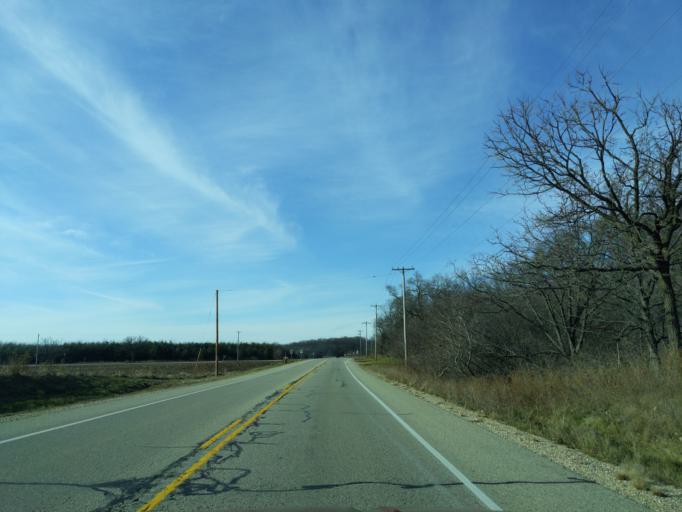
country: US
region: Wisconsin
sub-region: Jefferson County
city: Palmyra
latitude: 42.7976
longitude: -88.6384
